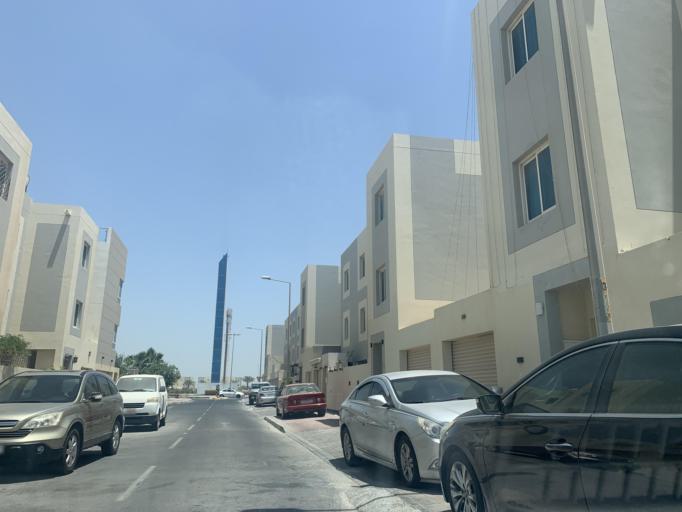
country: BH
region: Manama
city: Jidd Hafs
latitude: 26.2353
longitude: 50.4680
